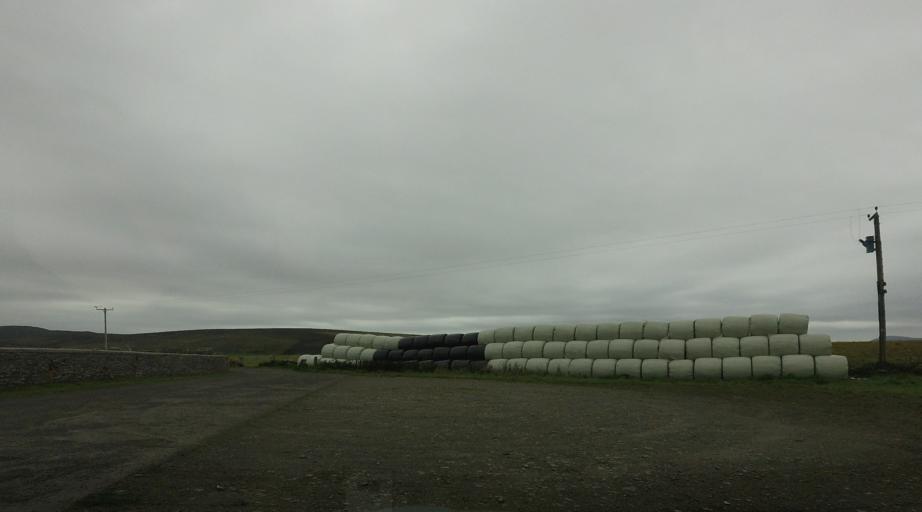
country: GB
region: Scotland
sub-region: Orkney Islands
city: Stromness
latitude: 58.9932
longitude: -3.2008
